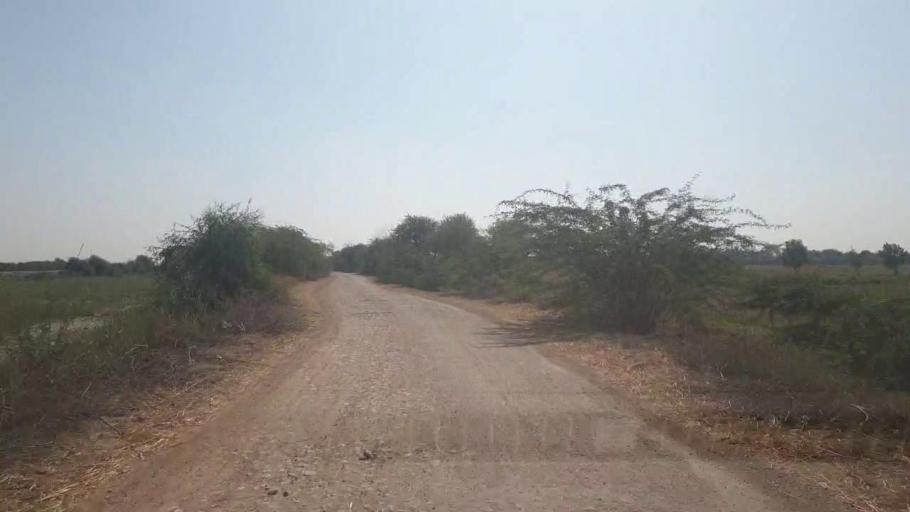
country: PK
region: Sindh
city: Badin
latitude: 24.6039
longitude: 68.8545
